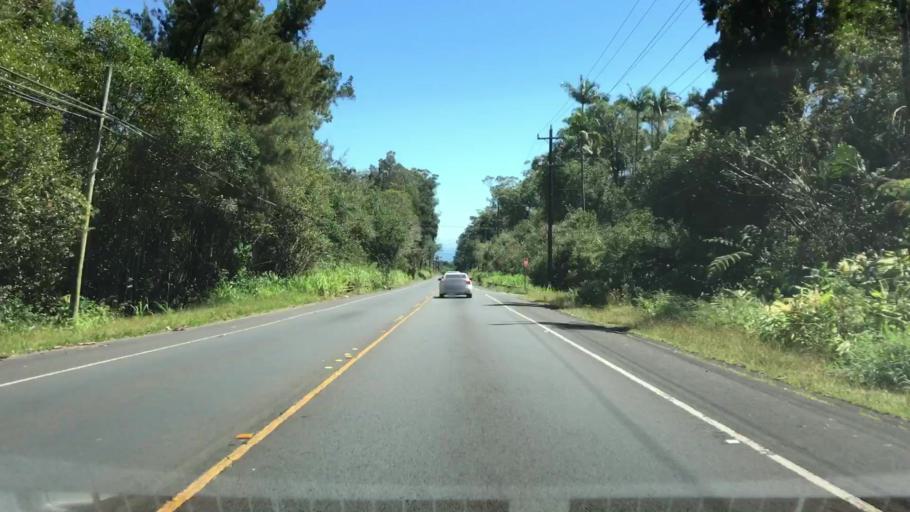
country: US
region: Hawaii
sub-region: Hawaii County
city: Mountain View
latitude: 19.5406
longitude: -155.1206
